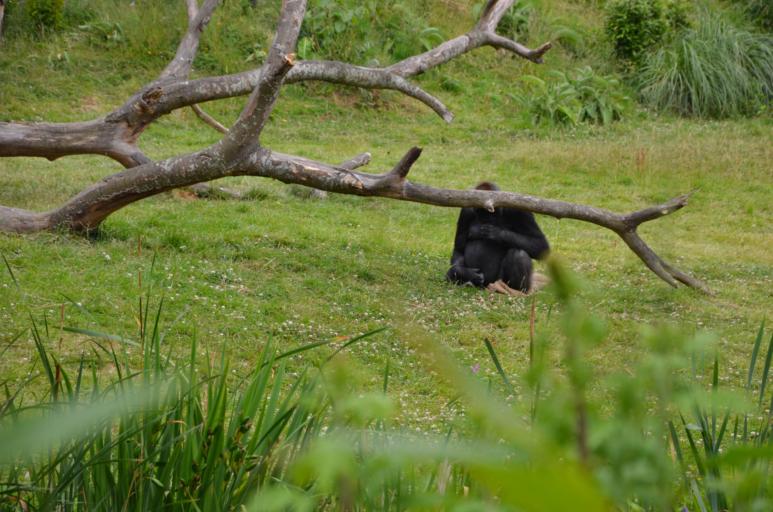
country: IE
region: Leinster
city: Cabra
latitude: 53.3590
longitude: -6.3100
